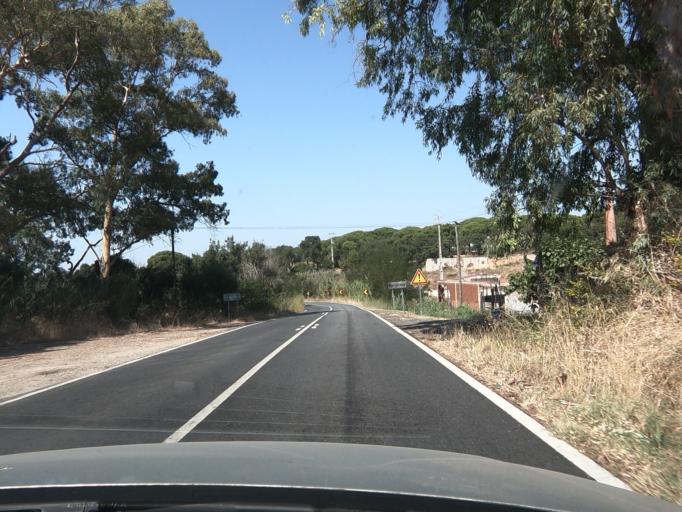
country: PT
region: Setubal
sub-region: Alcacer do Sal
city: Alcacer do Sal
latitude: 38.3608
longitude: -8.4776
